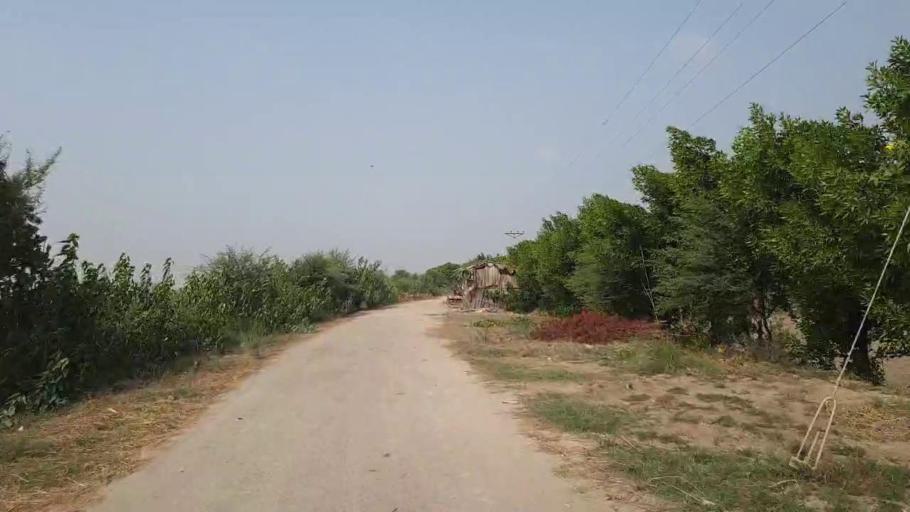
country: PK
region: Sindh
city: Kario
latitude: 24.8259
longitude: 68.5502
